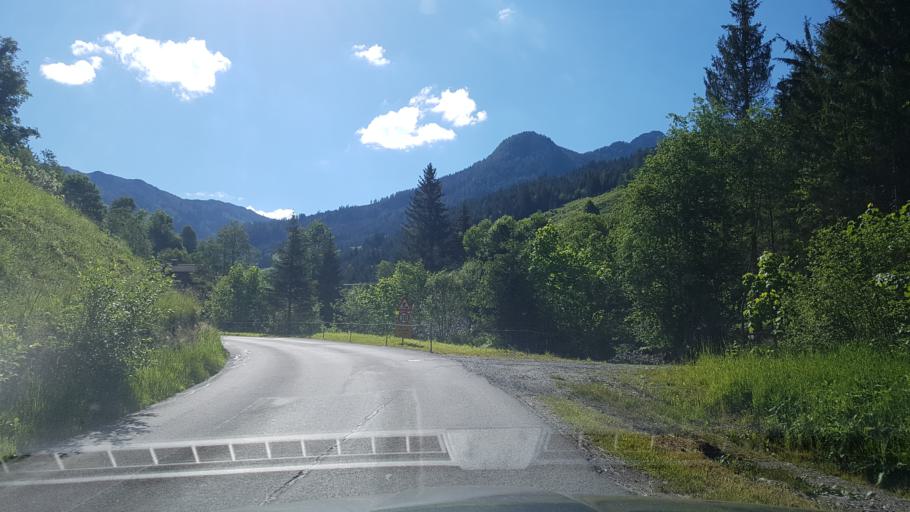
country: AT
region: Salzburg
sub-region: Politischer Bezirk Sankt Johann im Pongau
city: Huttschlag
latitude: 47.2361
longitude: 13.2336
